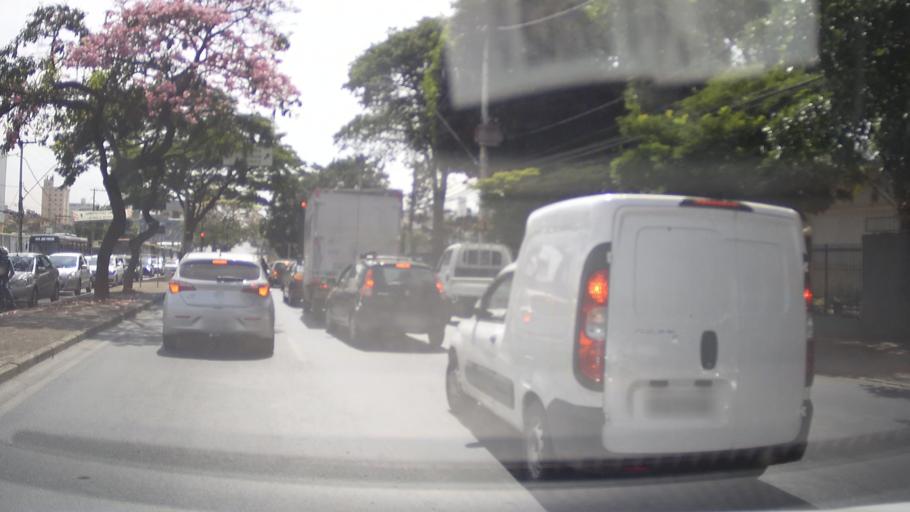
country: BR
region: Minas Gerais
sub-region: Belo Horizonte
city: Belo Horizonte
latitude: -19.9314
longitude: -43.9854
